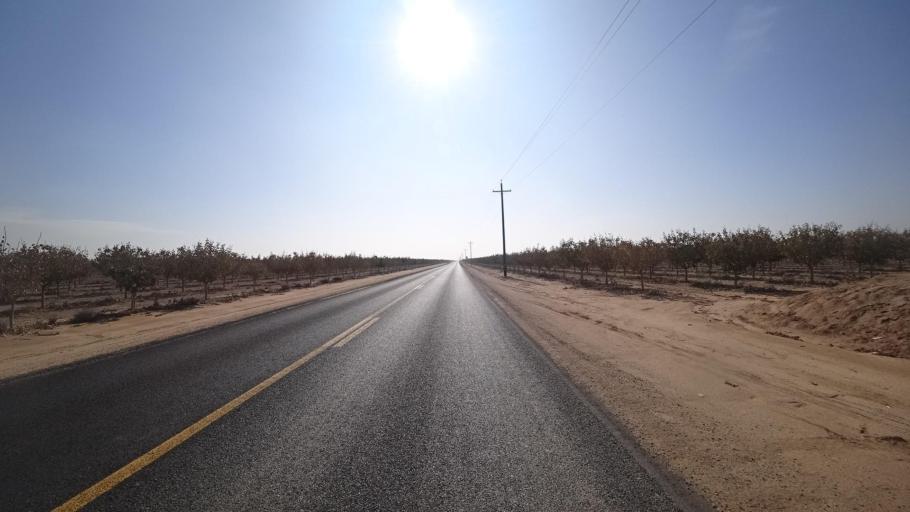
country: US
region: California
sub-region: Kern County
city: Shafter
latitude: 35.5436
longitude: -119.1513
